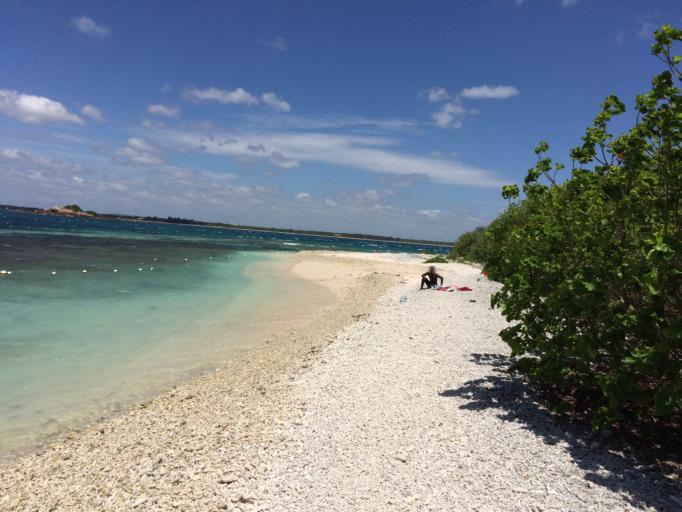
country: LK
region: Eastern Province
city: Trincomalee
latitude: 8.7216
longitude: 81.2041
